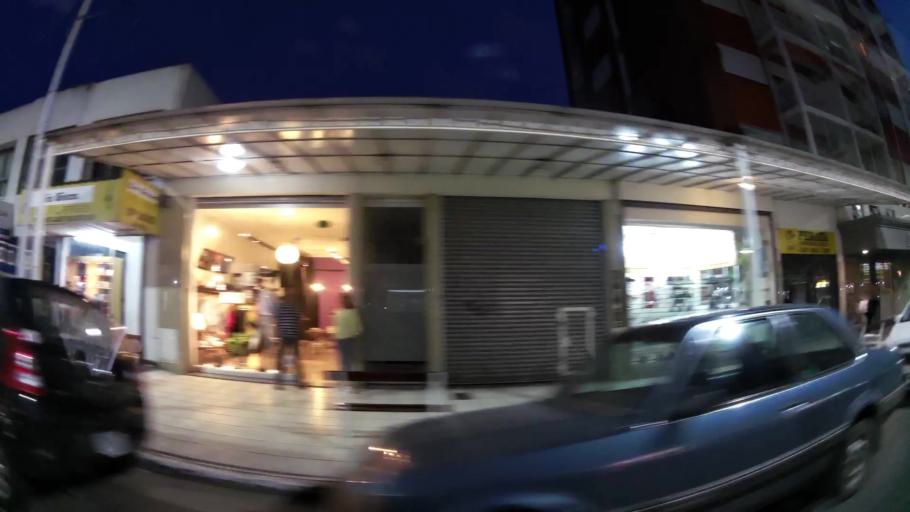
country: AR
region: Buenos Aires
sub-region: Partido de Quilmes
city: Quilmes
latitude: -34.6993
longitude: -58.3119
